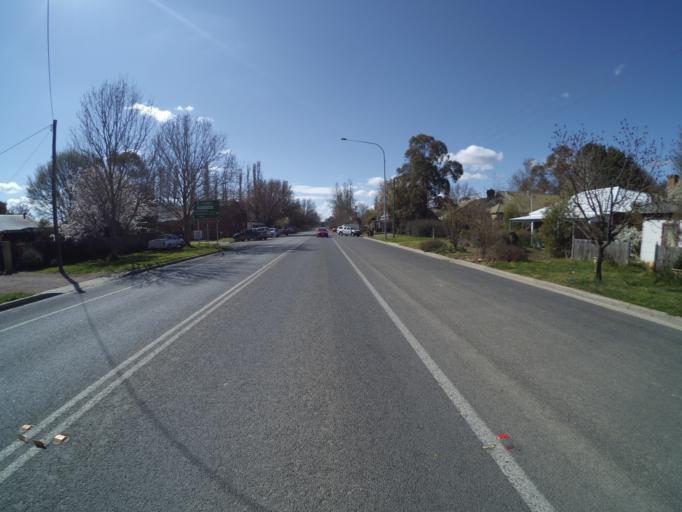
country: AU
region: New South Wales
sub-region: Palerang
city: Bungendore
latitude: -35.2570
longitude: 149.4377
